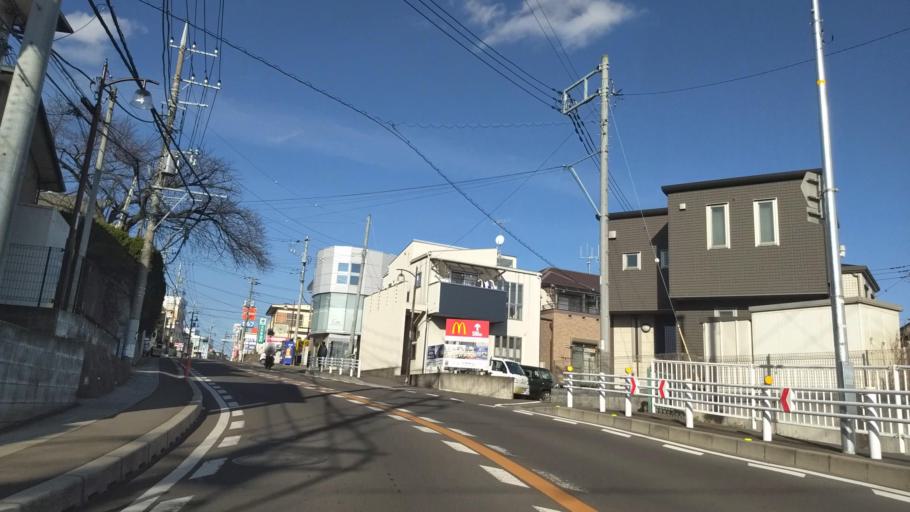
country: JP
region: Kanagawa
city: Isehara
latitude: 35.3740
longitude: 139.2762
